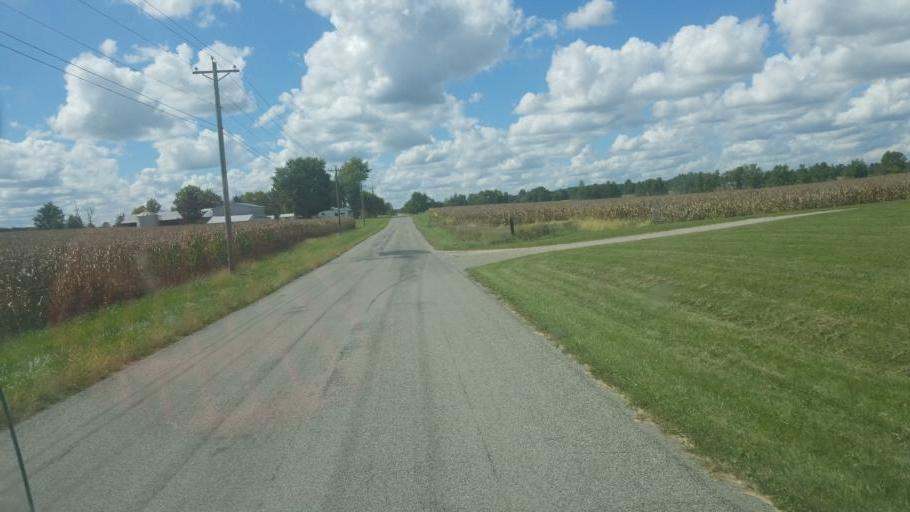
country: US
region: Ohio
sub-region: Champaign County
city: North Lewisburg
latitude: 40.3282
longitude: -83.4870
